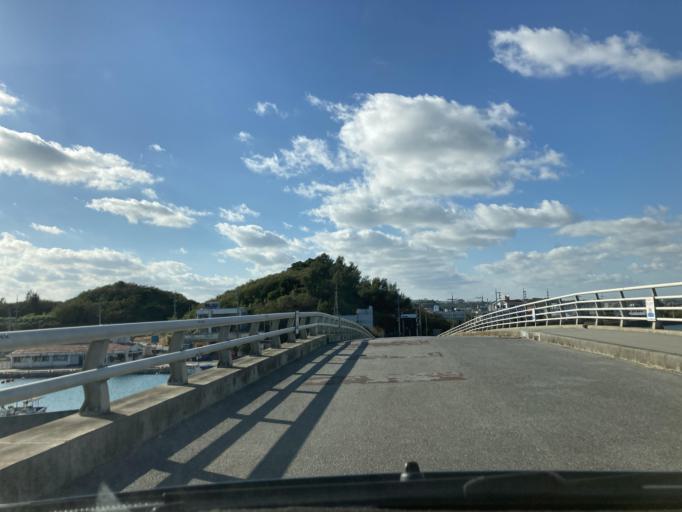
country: JP
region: Okinawa
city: Katsuren-haebaru
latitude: 26.3214
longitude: 127.9168
